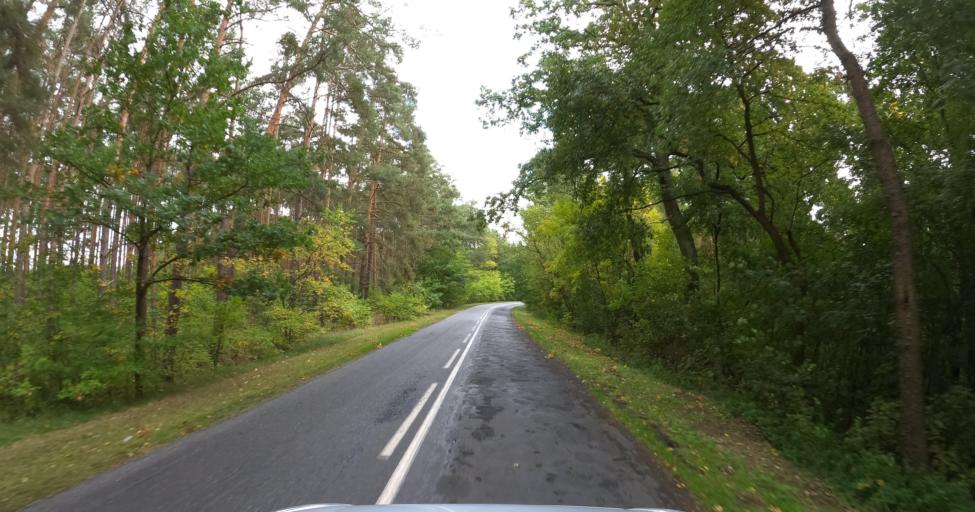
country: PL
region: Lubusz
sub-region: Powiat zielonogorski
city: Zabor
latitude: 51.9711
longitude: 15.6165
